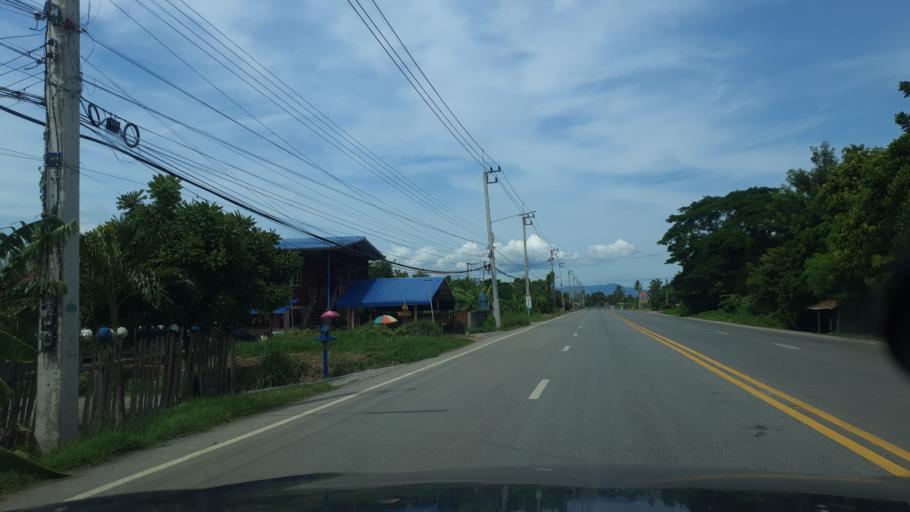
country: TH
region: Sukhothai
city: Sukhothai
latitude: 17.0554
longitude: 99.8226
